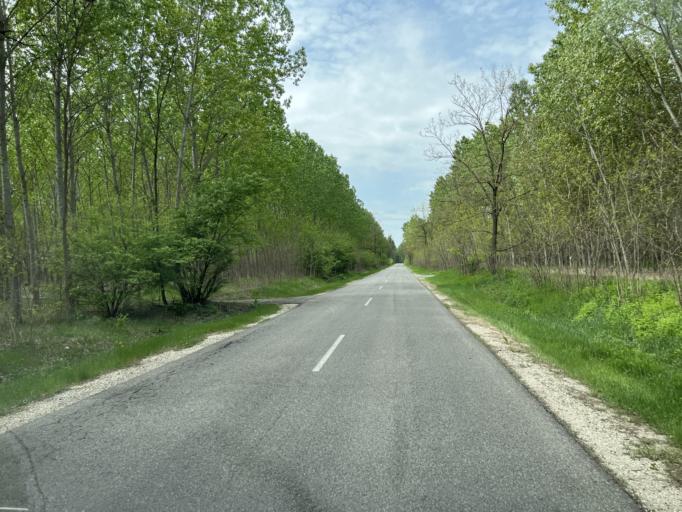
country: HU
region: Pest
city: Csemo
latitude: 47.1330
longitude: 19.6505
